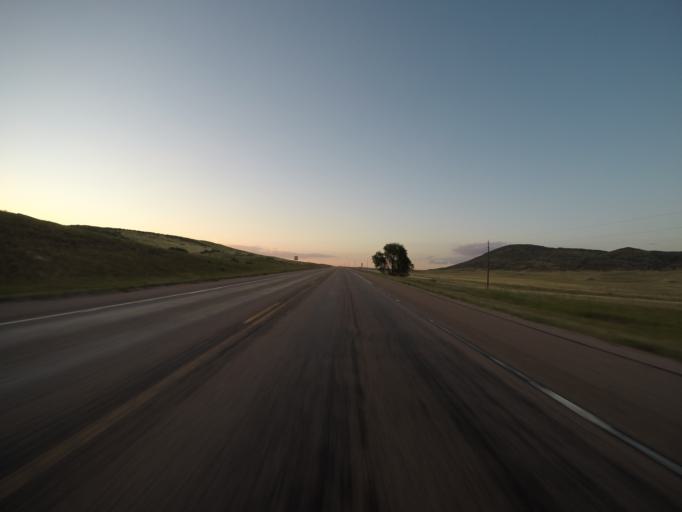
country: US
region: Colorado
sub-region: Larimer County
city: Laporte
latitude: 40.7437
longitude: -105.1706
